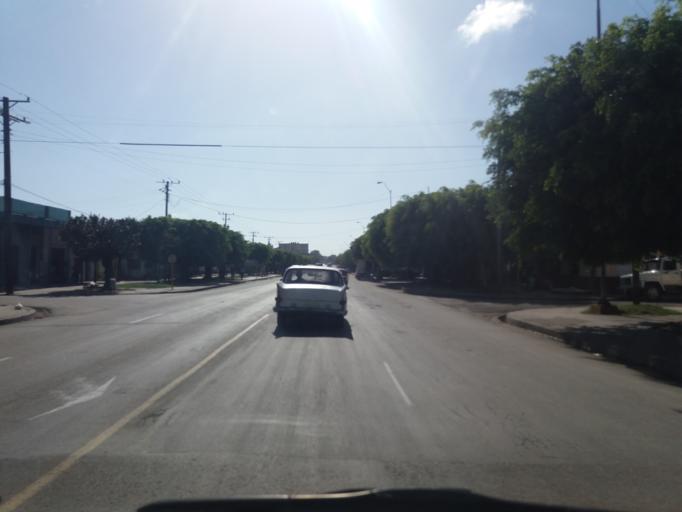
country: CU
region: Cienfuegos
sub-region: Municipio de Cienfuegos
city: Cienfuegos
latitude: 22.1526
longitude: -80.4380
